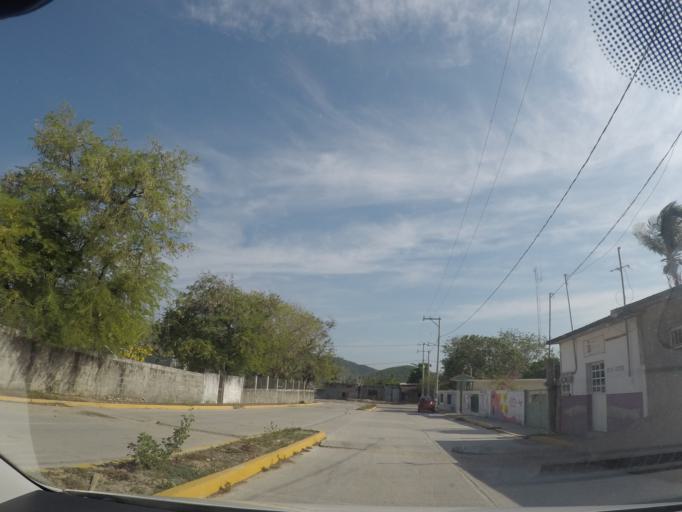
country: MX
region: Oaxaca
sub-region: Salina Cruz
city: Salina Cruz
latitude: 16.2200
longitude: -95.1294
